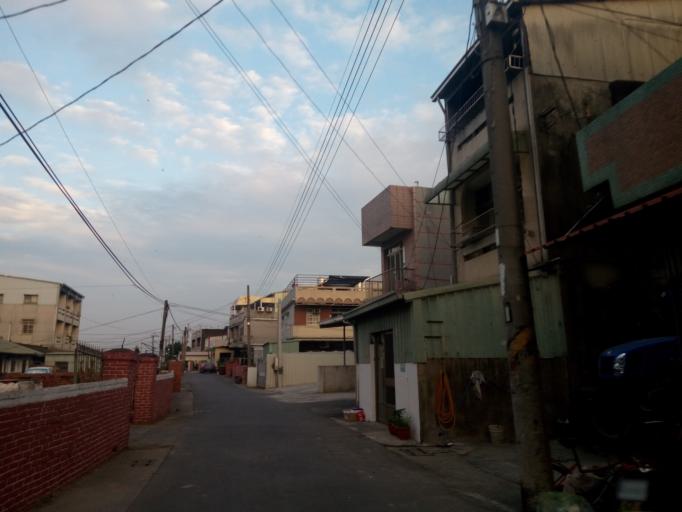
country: TW
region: Taiwan
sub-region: Chiayi
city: Jiayi Shi
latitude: 23.5000
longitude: 120.3867
